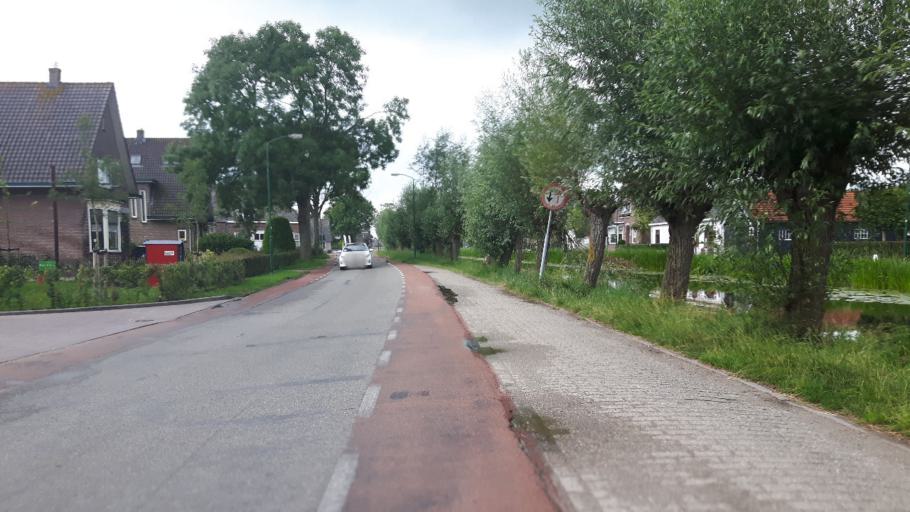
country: NL
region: South Holland
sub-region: Gemeente Schoonhoven
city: Schoonhoven
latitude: 51.9774
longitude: 4.8522
